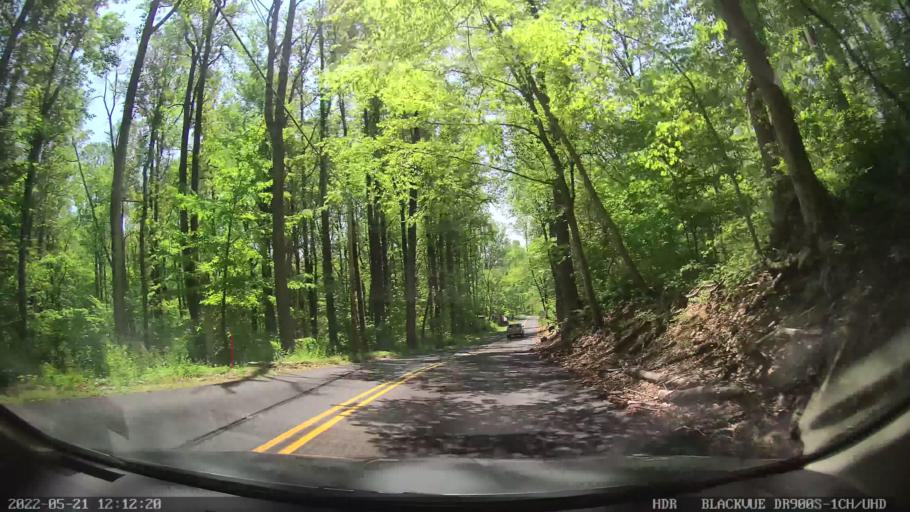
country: US
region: Pennsylvania
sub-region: Berks County
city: Topton
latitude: 40.4489
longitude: -75.6778
